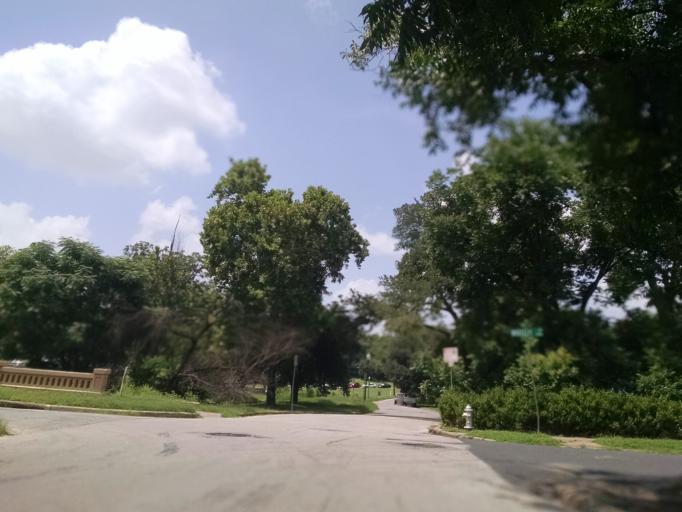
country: US
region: Texas
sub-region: Travis County
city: Austin
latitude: 30.2970
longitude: -97.7394
